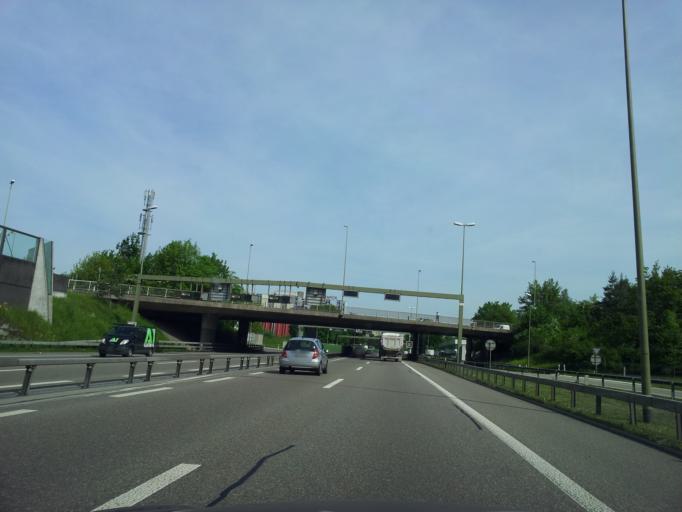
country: CH
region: Zurich
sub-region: Bezirk Buelach
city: Glattbrugg / Rohr/Platten-Balsberg
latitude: 47.4367
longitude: 8.5706
